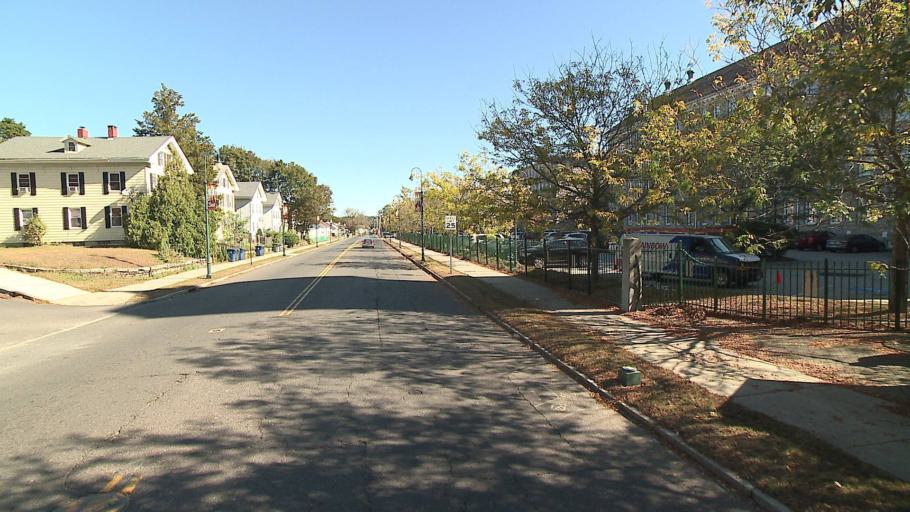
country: US
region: Connecticut
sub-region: Windham County
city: Willimantic
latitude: 41.7113
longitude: -72.2046
